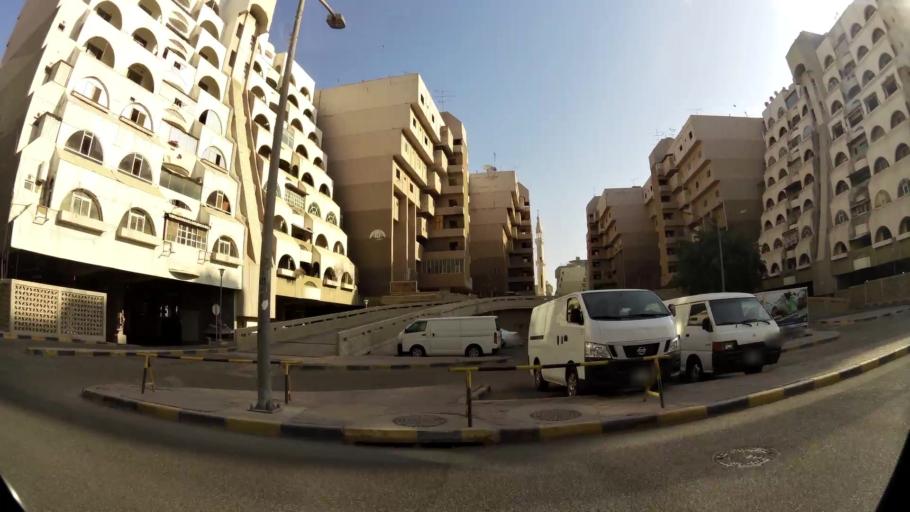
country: KW
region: Al Asimah
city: Kuwait City
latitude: 29.3748
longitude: 47.9805
